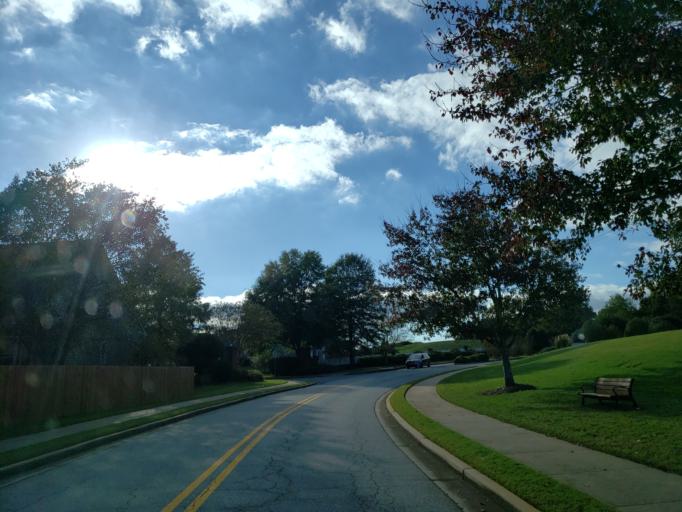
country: US
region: Georgia
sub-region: Cobb County
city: Marietta
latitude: 33.9884
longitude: -84.5054
